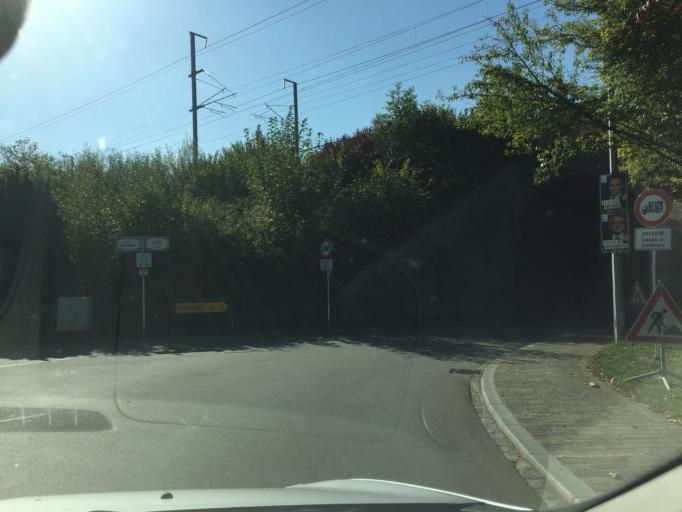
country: LU
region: Luxembourg
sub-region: Canton de Capellen
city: Mamer
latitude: 49.6232
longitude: 6.0235
